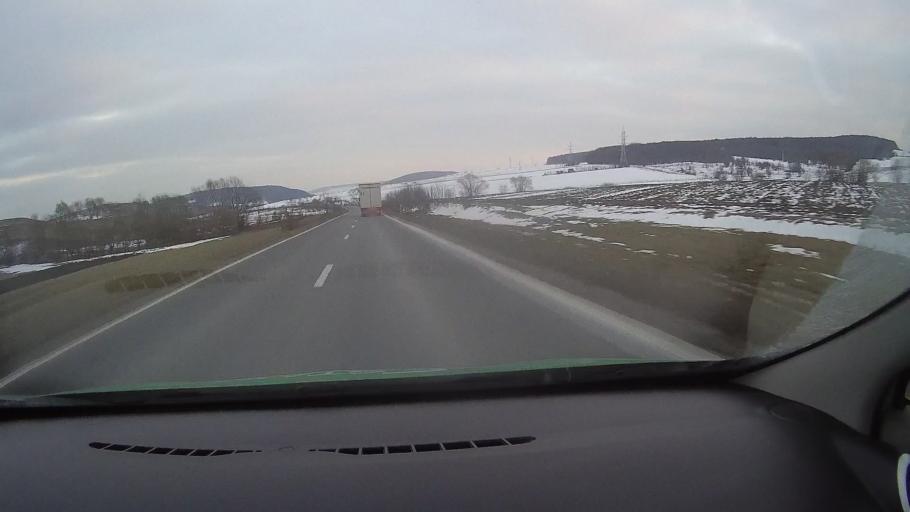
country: RO
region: Harghita
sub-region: Comuna Lupeni
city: Lupeni
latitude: 46.3550
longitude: 25.2531
